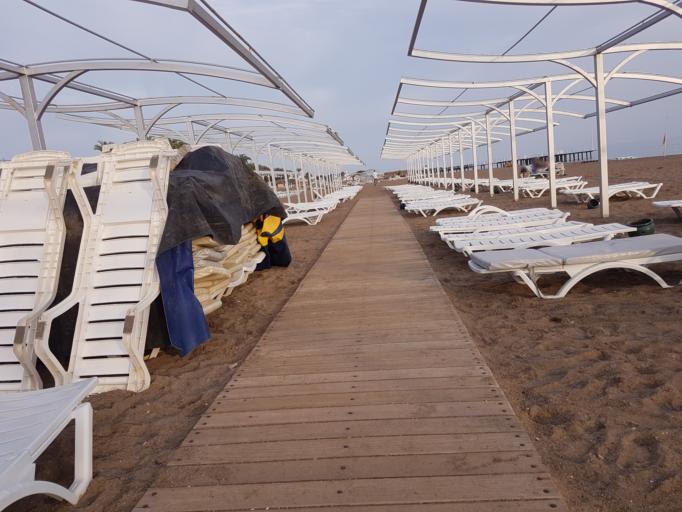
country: TR
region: Antalya
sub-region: Serik
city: Kumkoey
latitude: 36.8518
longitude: 30.8586
